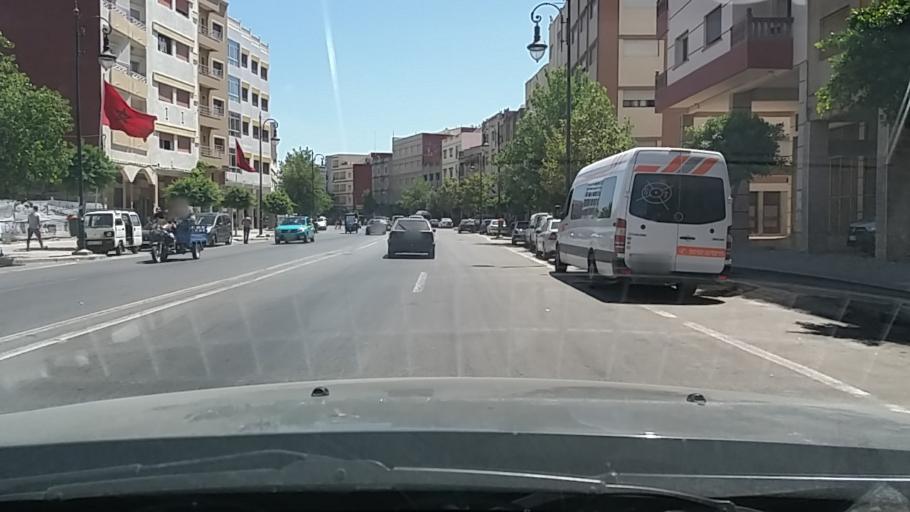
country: MA
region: Tanger-Tetouan
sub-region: Tanger-Assilah
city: Tangier
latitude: 35.7519
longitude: -5.8039
